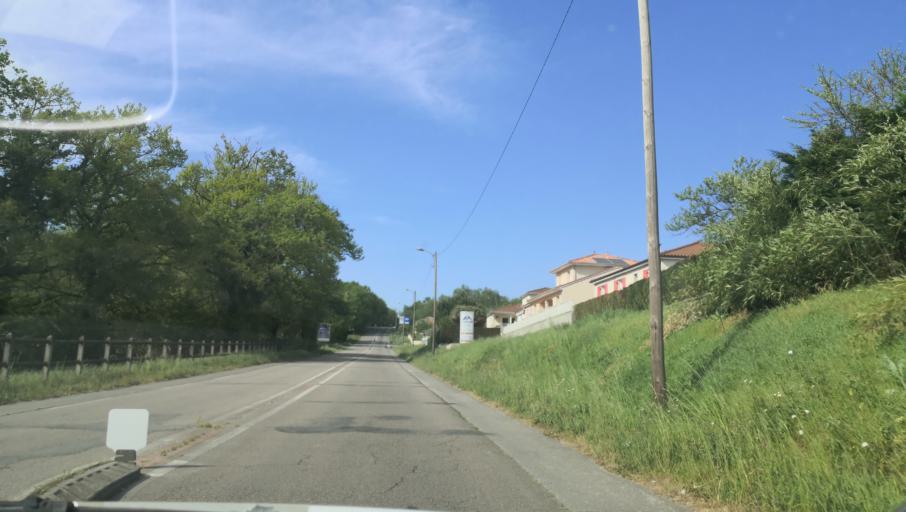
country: FR
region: Limousin
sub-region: Departement de la Haute-Vienne
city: Couzeix
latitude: 45.8633
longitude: 1.2590
